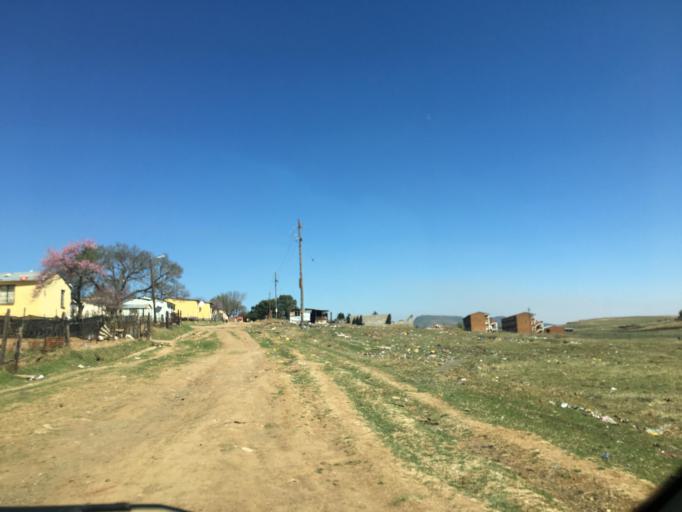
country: ZA
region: Eastern Cape
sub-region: Chris Hani District Municipality
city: Elliot
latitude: -31.3272
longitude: 27.8252
